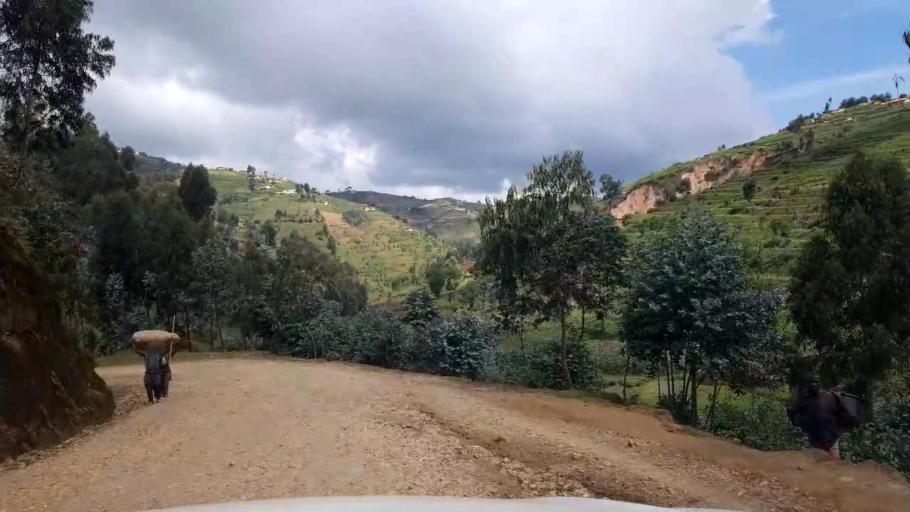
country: RW
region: Western Province
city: Kibuye
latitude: -1.8929
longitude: 29.4621
